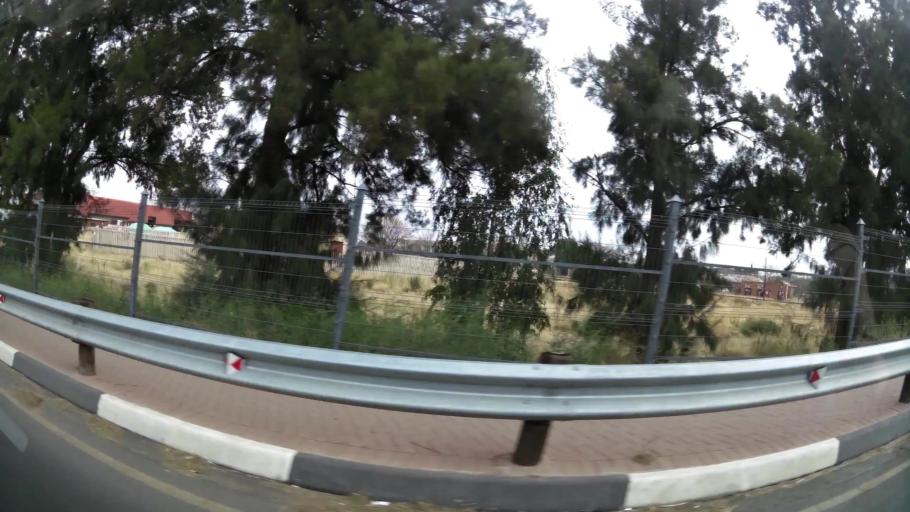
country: ZA
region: Orange Free State
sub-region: Mangaung Metropolitan Municipality
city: Bloemfontein
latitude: -29.1333
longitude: 26.2068
